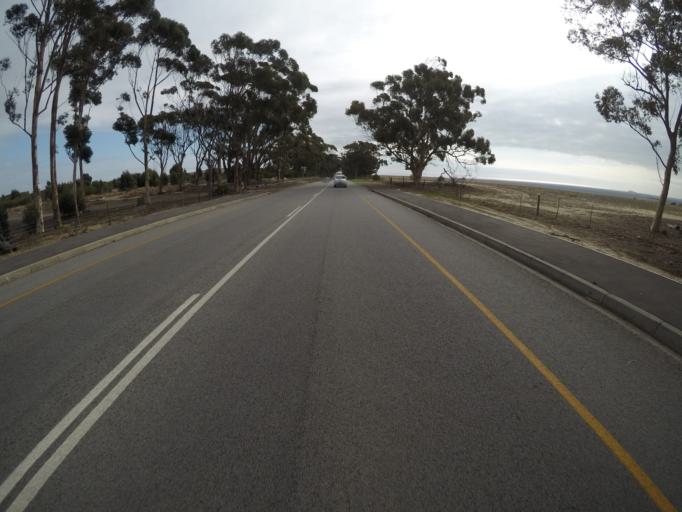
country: ZA
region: Western Cape
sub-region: City of Cape Town
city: Sunset Beach
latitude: -33.7219
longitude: 18.5074
